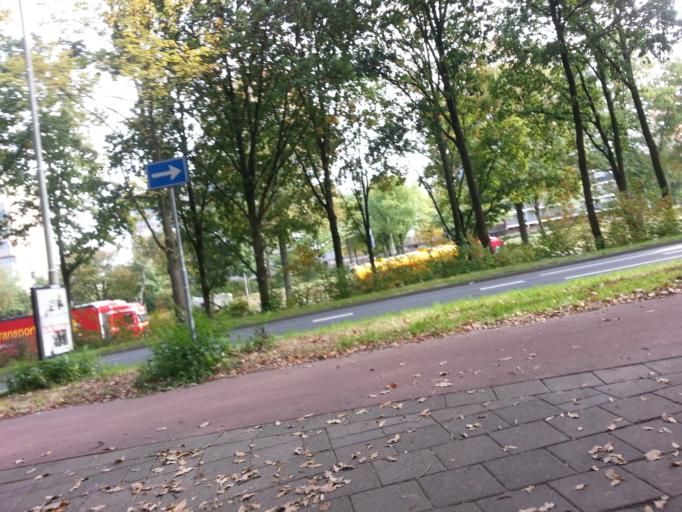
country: NL
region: North Brabant
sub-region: Gemeente Eindhoven
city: Villapark
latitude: 51.4687
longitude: 5.4862
